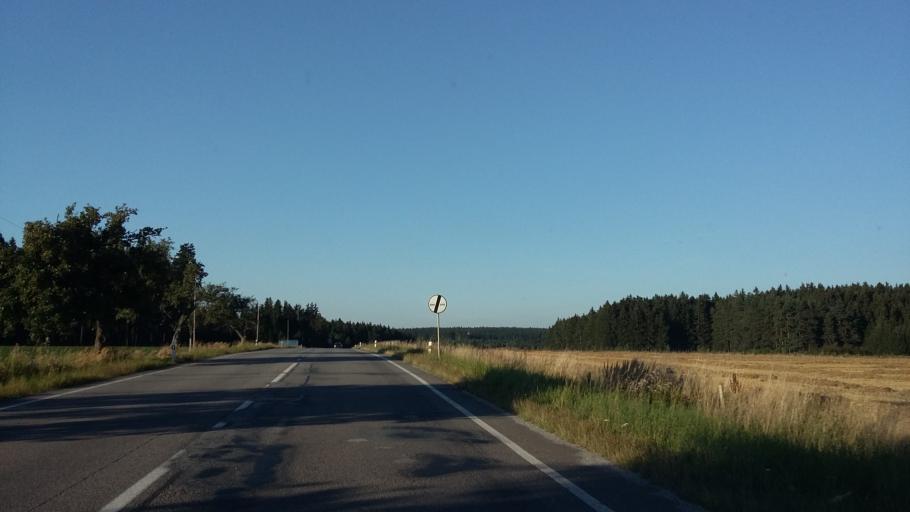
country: CZ
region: Vysocina
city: Velky Beranov
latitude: 49.4120
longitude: 15.6718
